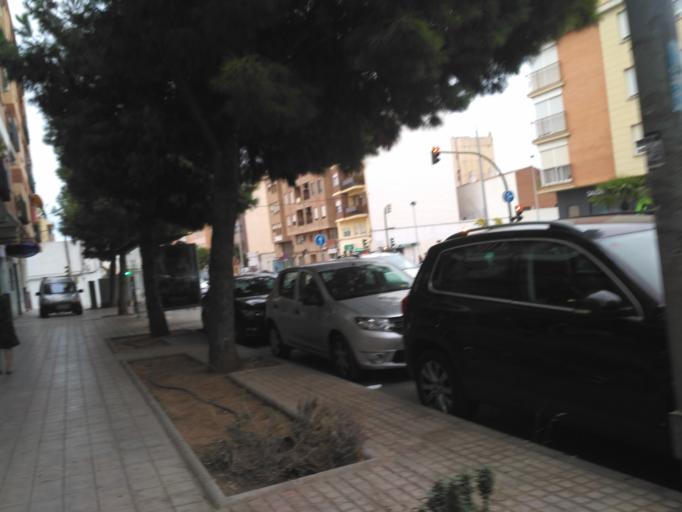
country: ES
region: Valencia
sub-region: Provincia de Castello
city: Castello de la Plana
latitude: 39.9869
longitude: -0.0588
